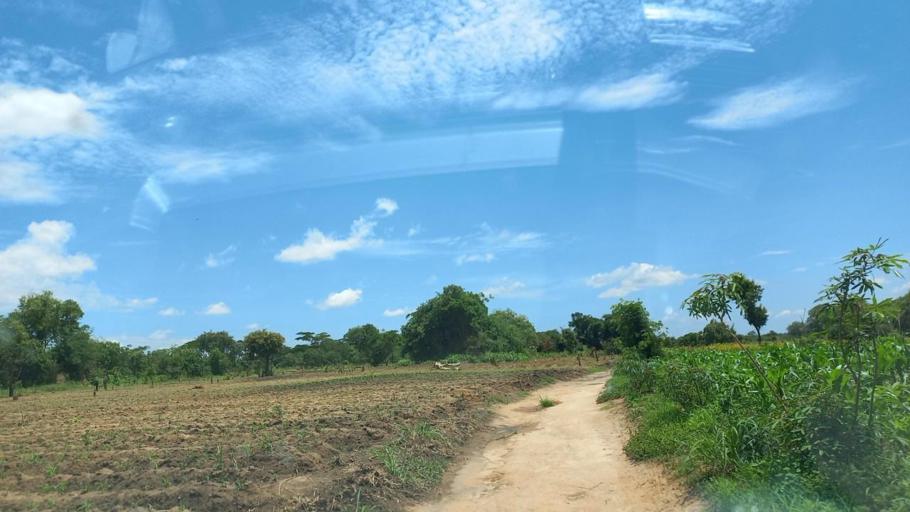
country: ZM
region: Copperbelt
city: Ndola
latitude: -12.8778
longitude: 28.4455
